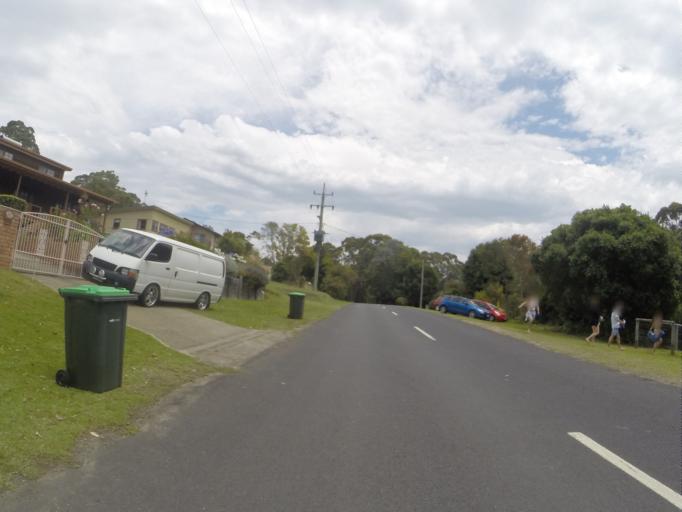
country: AU
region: New South Wales
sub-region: Eurobodalla
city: Batemans Bay
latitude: -35.6669
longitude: 150.2970
